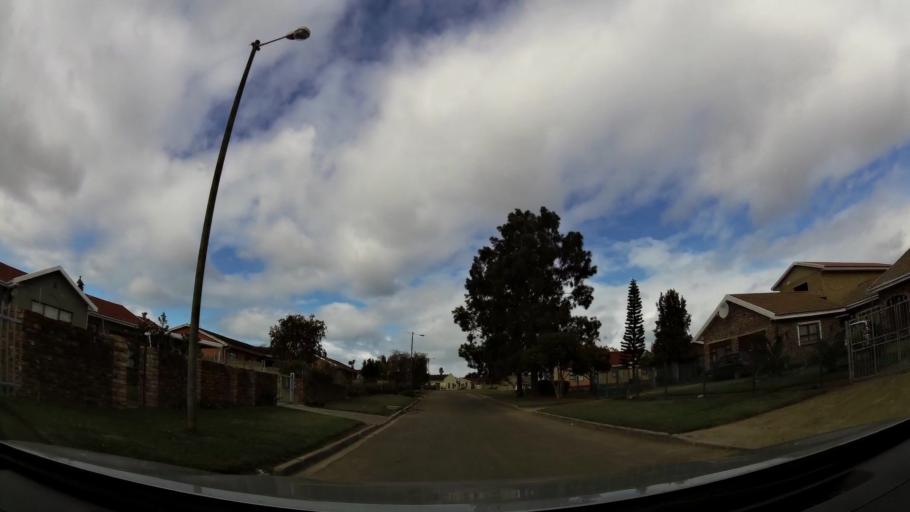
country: ZA
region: Western Cape
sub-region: Eden District Municipality
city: George
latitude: -34.0048
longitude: 22.4428
